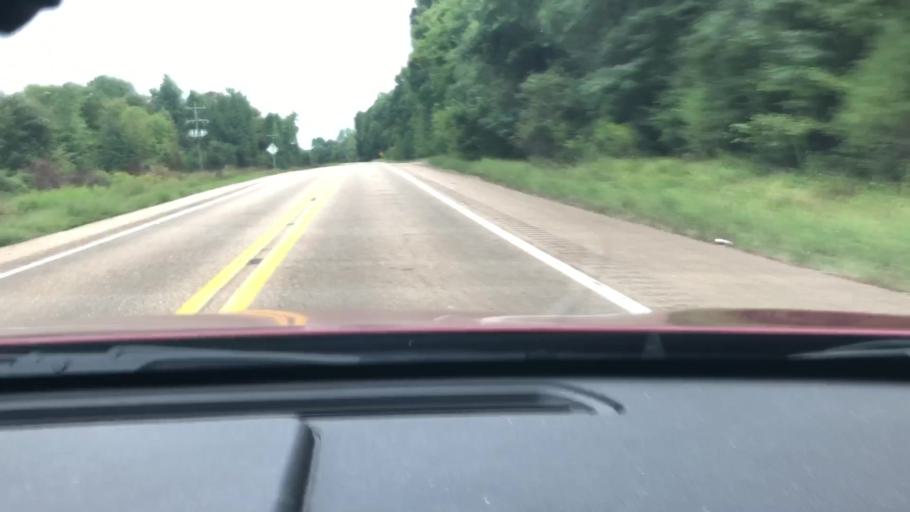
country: US
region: Arkansas
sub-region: Miller County
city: Texarkana
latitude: 33.4171
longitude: -93.8129
